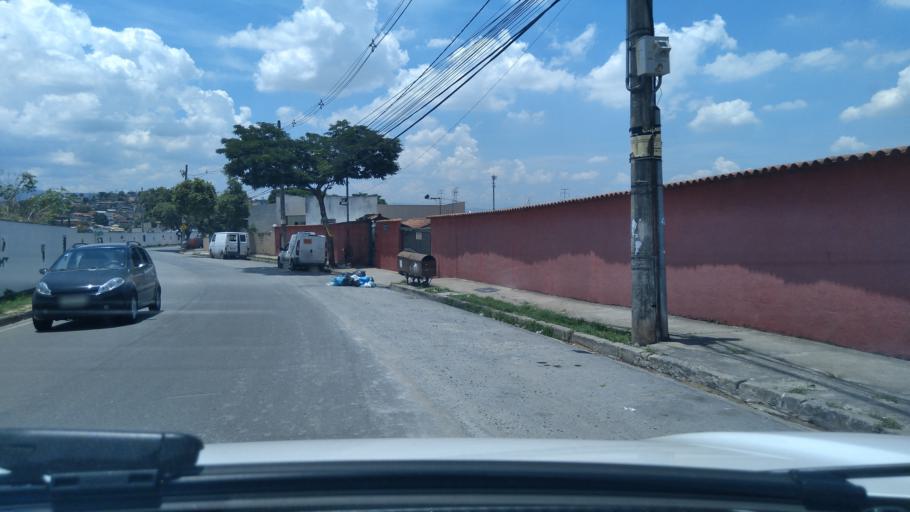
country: BR
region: Minas Gerais
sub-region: Contagem
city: Contagem
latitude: -19.9284
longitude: -44.0163
